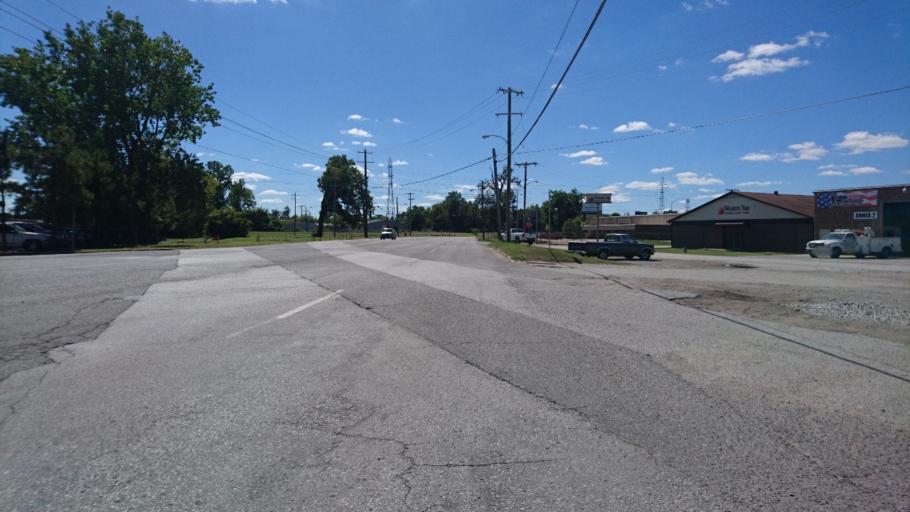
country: US
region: Oklahoma
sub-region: Tulsa County
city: Tulsa
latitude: 36.1140
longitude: -96.0093
